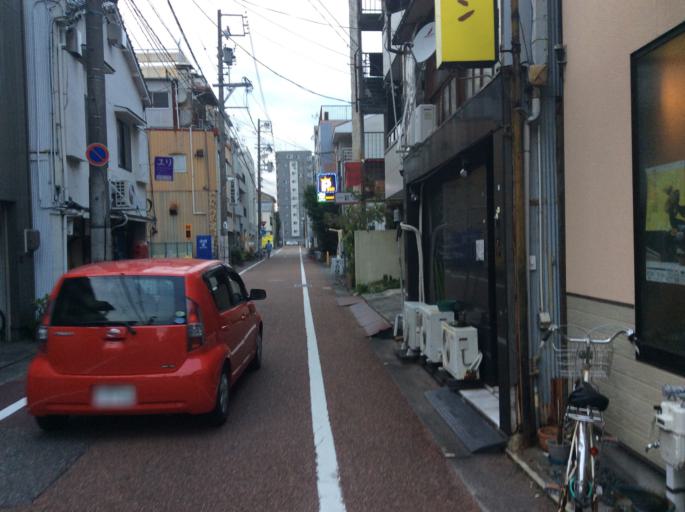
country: JP
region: Shizuoka
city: Shizuoka-shi
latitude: 34.9735
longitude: 138.3793
